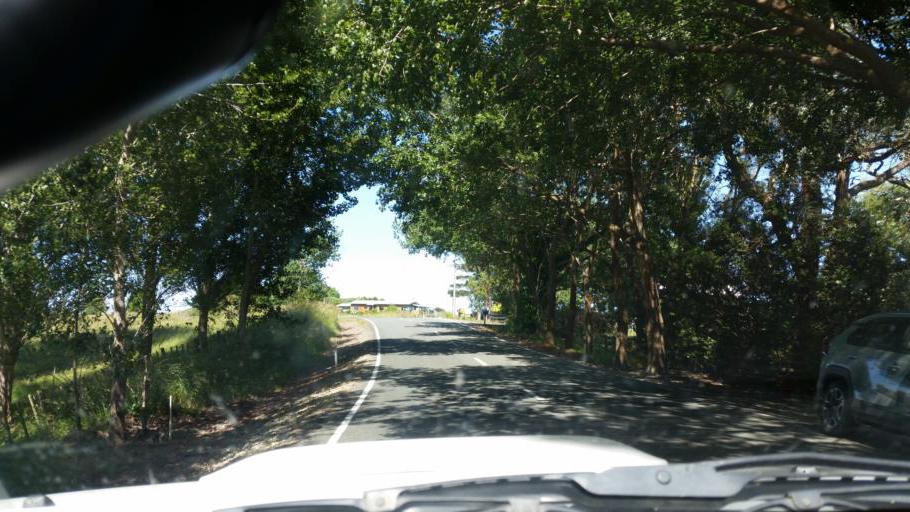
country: NZ
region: Auckland
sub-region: Auckland
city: Wellsford
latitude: -36.2187
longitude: 174.3833
